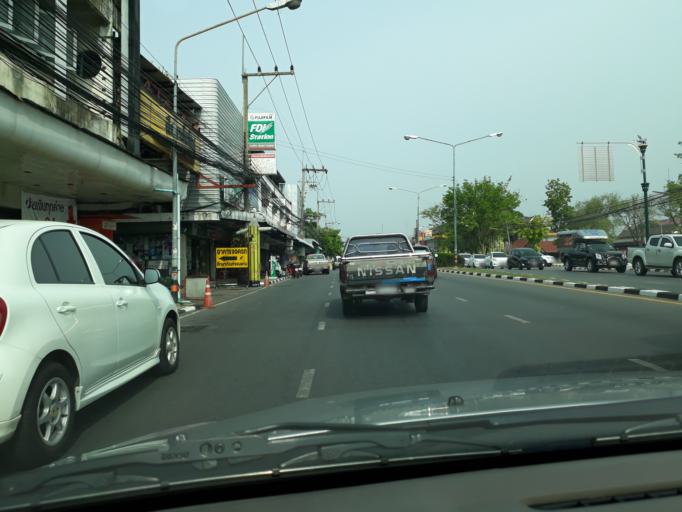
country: TH
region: Khon Kaen
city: Khon Kaen
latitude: 16.4385
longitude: 102.8361
